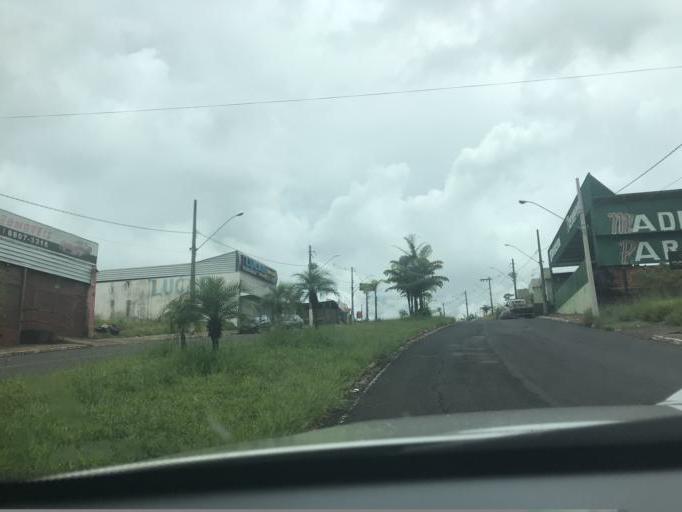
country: BR
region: Minas Gerais
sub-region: Araxa
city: Araxa
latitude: -19.5802
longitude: -46.9385
